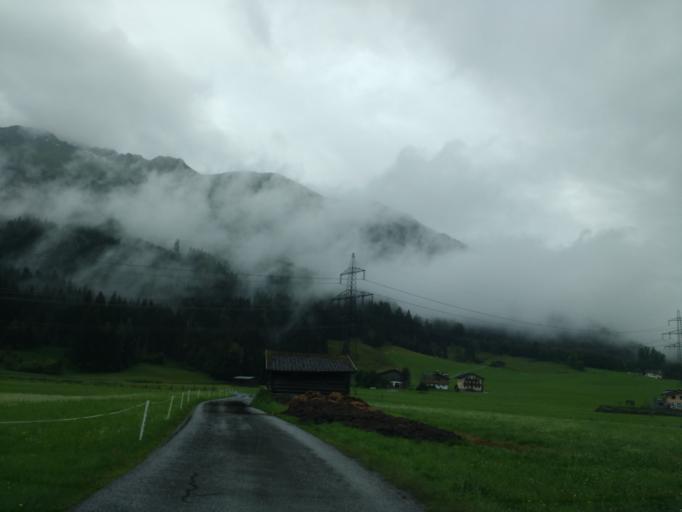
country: AT
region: Salzburg
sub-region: Politischer Bezirk Zell am See
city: Neukirchen am Grossvenediger
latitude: 47.2517
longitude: 12.2963
